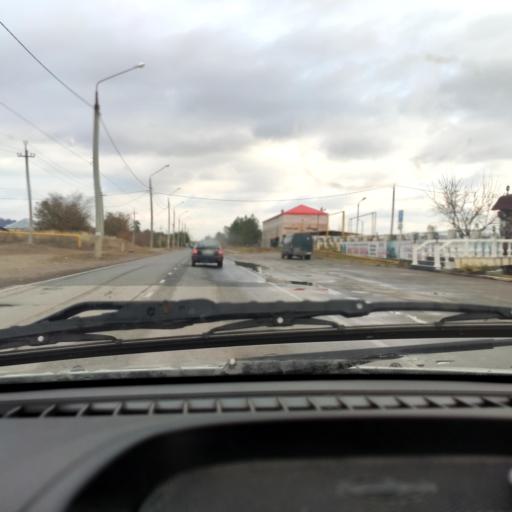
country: RU
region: Samara
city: Zhigulevsk
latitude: 53.4645
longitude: 49.5933
